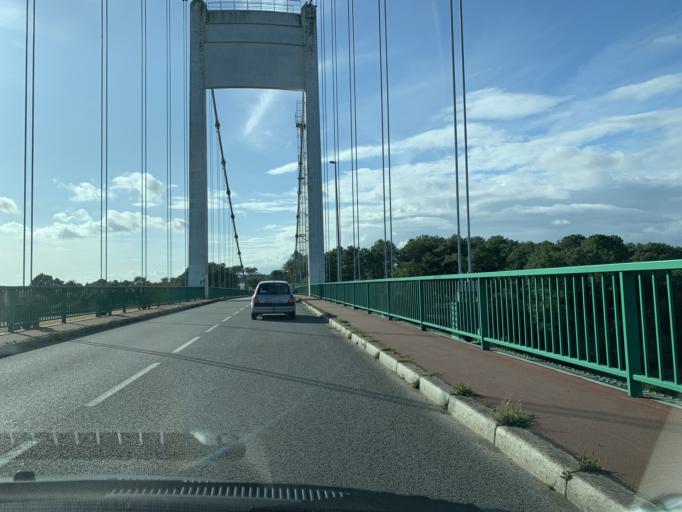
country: FR
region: Brittany
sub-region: Departement du Morbihan
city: Nivillac
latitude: 47.5243
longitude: -2.3047
